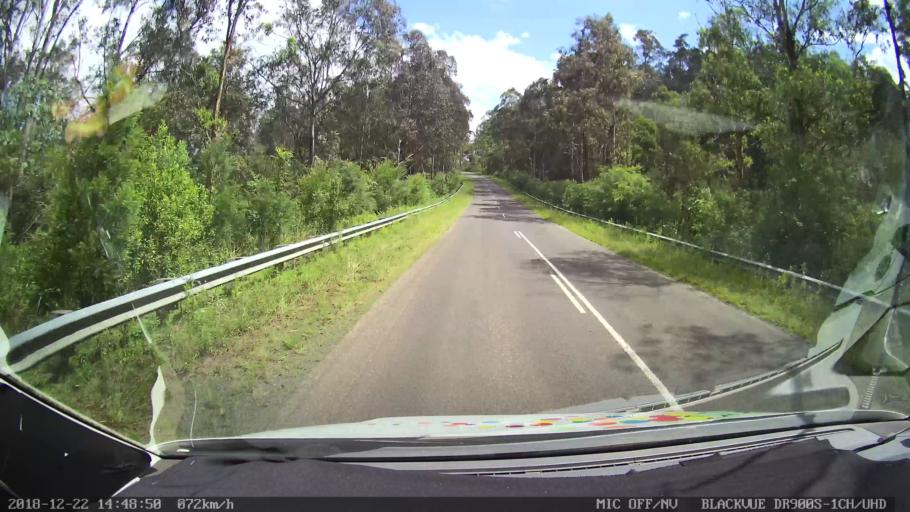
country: AU
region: New South Wales
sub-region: Bellingen
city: Dorrigo
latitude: -30.1842
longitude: 152.5514
